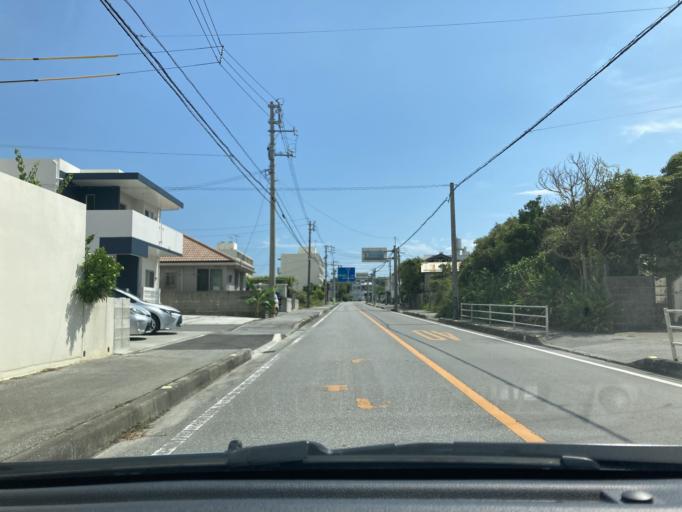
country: JP
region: Okinawa
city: Tomigusuku
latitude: 26.1794
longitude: 127.7212
